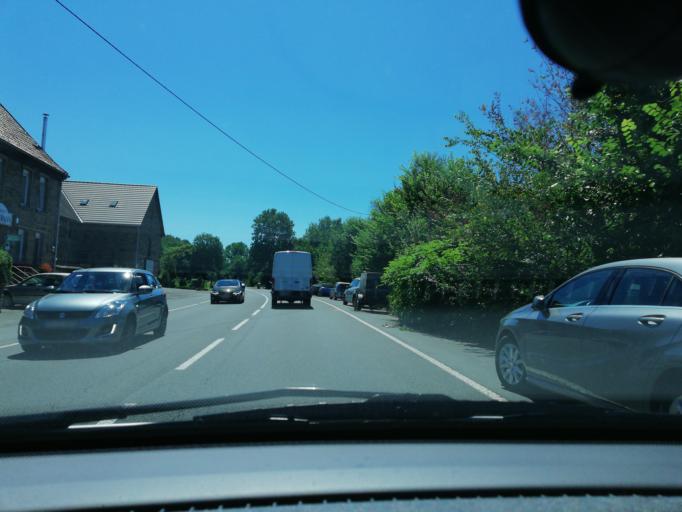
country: DE
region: North Rhine-Westphalia
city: Witten
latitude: 51.4113
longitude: 7.3530
